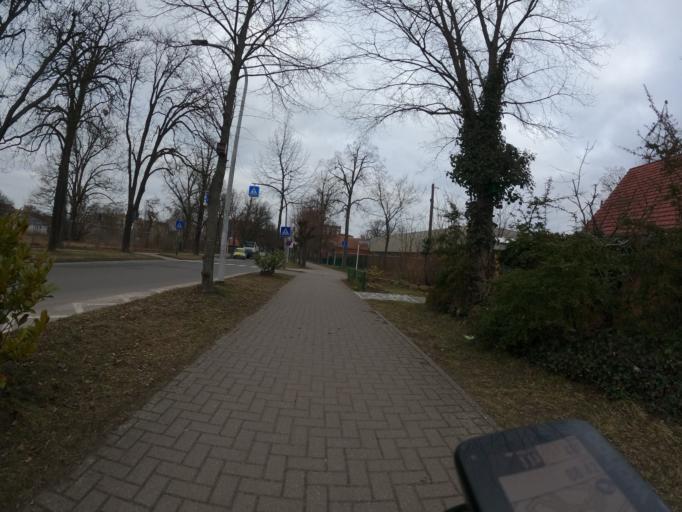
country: DE
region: Brandenburg
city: Strausberg
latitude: 52.5730
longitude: 13.8831
